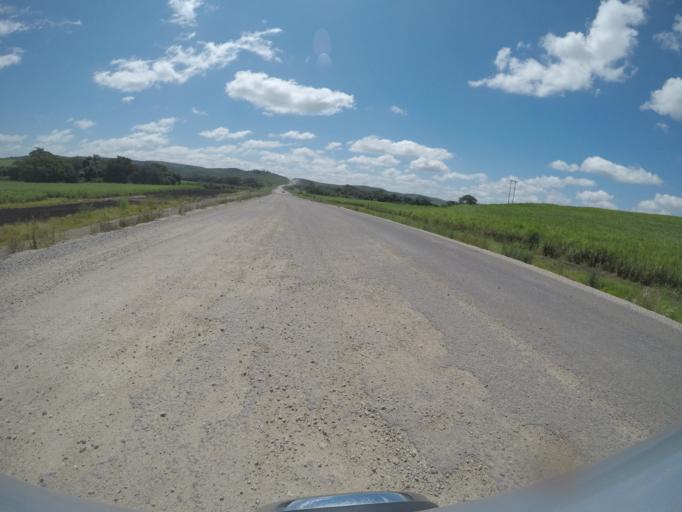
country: ZA
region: KwaZulu-Natal
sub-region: uThungulu District Municipality
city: Empangeni
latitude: -28.6496
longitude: 31.7688
